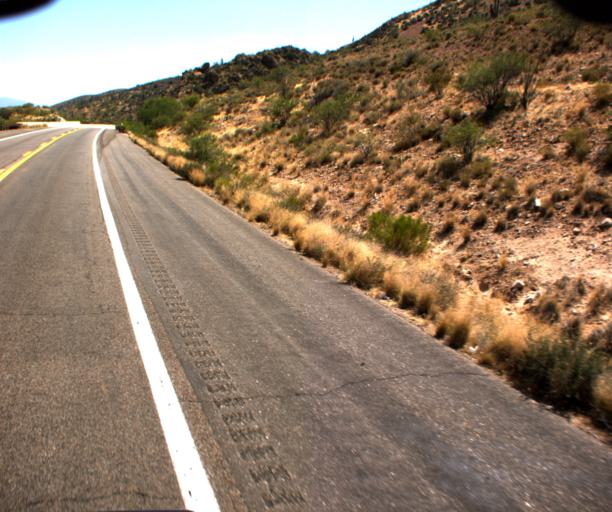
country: US
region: Arizona
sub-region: Gila County
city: Claypool
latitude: 33.5143
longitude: -110.8688
